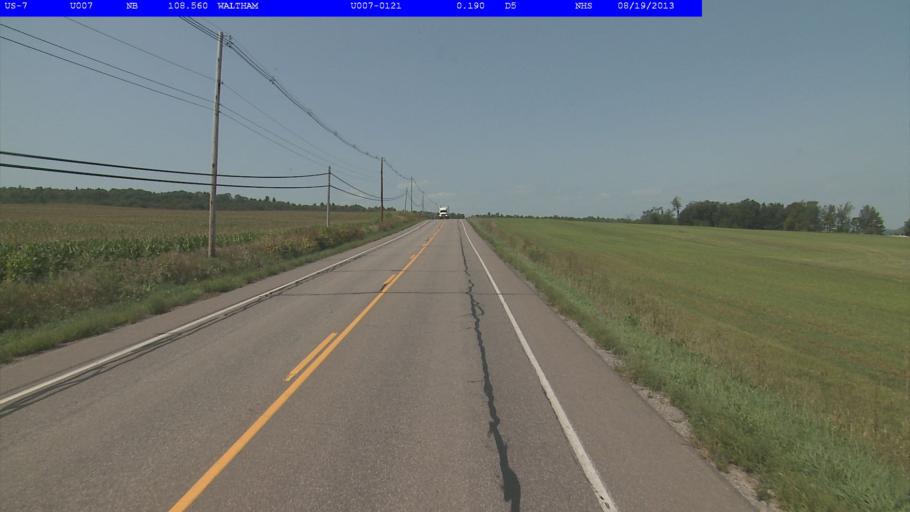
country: US
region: Vermont
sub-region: Addison County
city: Vergennes
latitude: 44.1497
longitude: -73.2127
